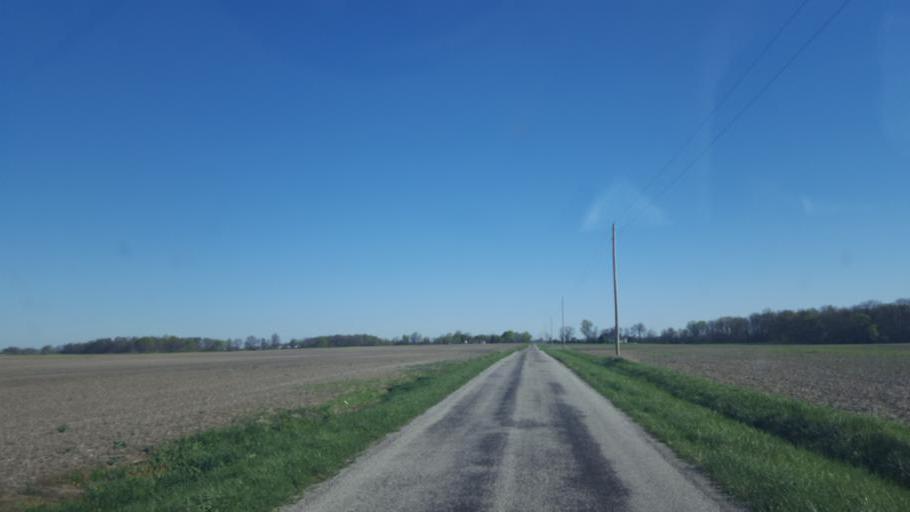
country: US
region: Ohio
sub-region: Crawford County
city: Bucyrus
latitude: 40.6535
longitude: -82.9817
